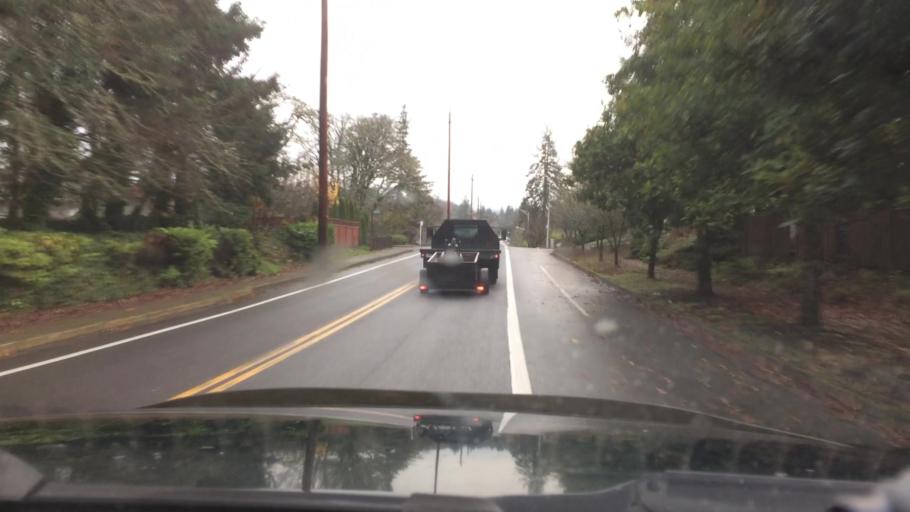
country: US
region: Oregon
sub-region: Lane County
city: Eugene
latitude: 44.0277
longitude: -123.1152
